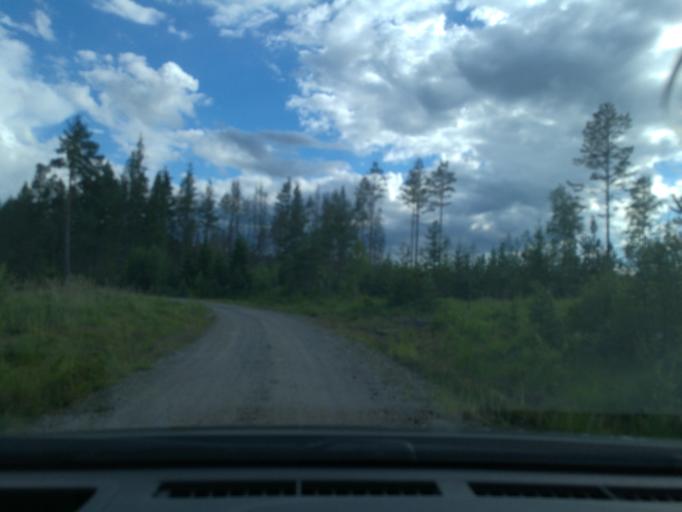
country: SE
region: Vaestmanland
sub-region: Surahammars Kommun
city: Ramnas
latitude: 59.8394
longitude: 16.2757
